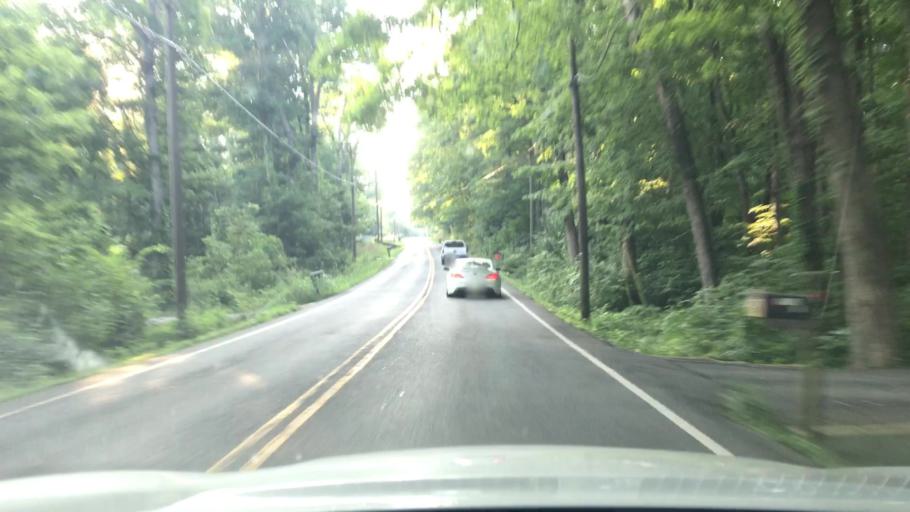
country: US
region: Tennessee
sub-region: Williamson County
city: Nolensville
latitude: 35.9910
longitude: -86.6450
